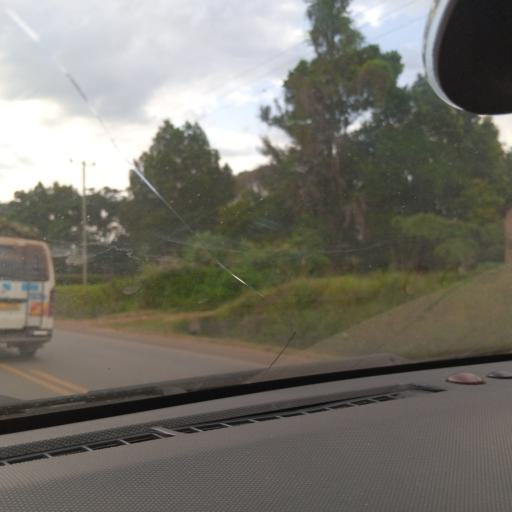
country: UG
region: Central Region
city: Masaka
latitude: -0.3366
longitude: 31.6944
